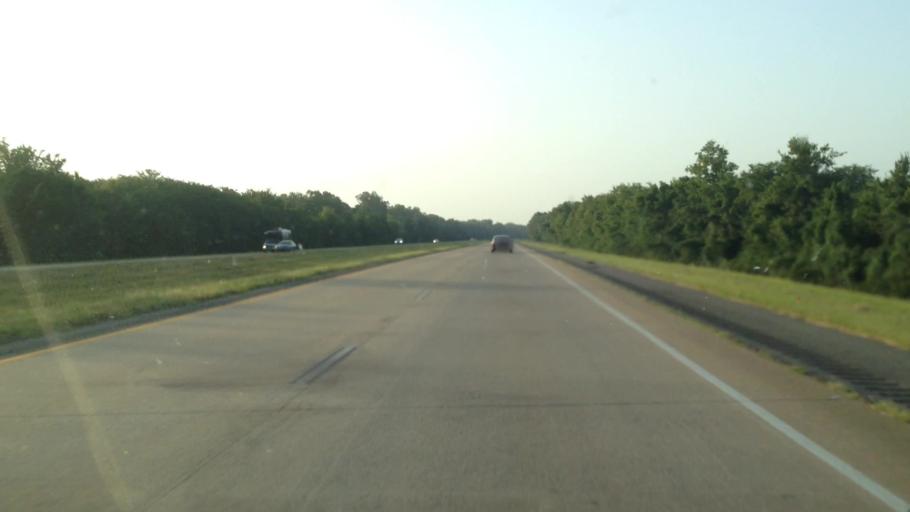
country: US
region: Louisiana
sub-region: Natchitoches Parish
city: Vienna Bend
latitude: 31.5521
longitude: -92.9719
